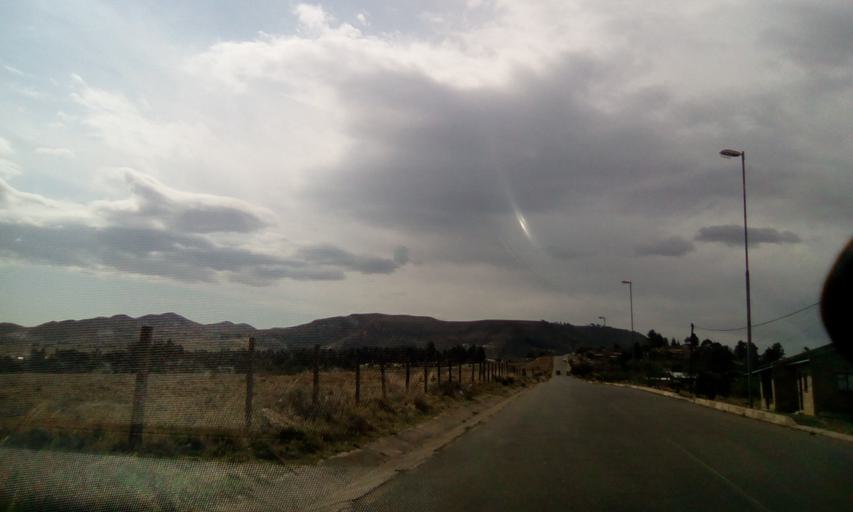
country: LS
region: Qacha's Nek
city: Qacha's Nek
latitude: -30.1110
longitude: 28.6705
